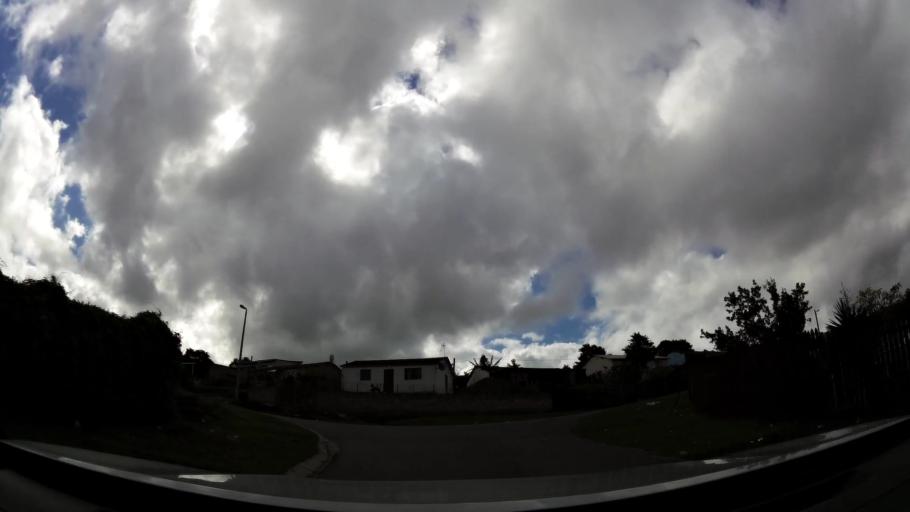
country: ZA
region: Western Cape
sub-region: Eden District Municipality
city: Knysna
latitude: -34.0521
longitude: 23.0985
